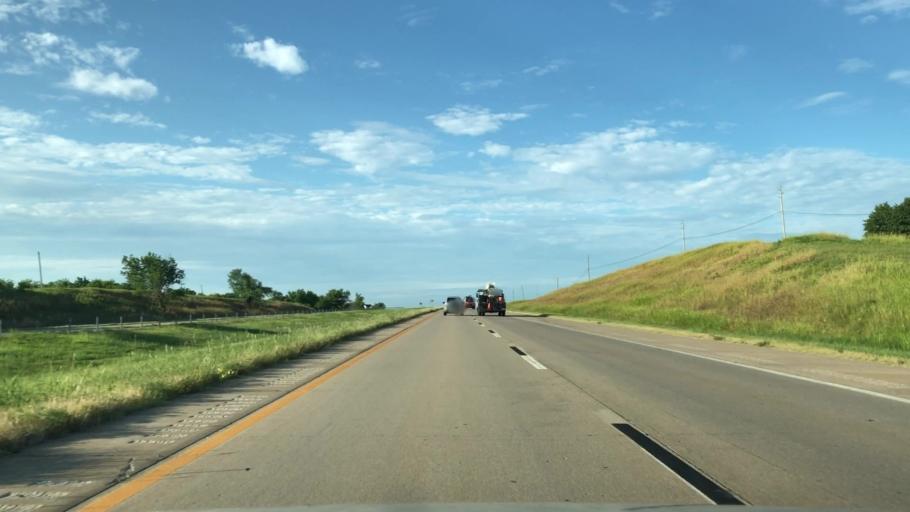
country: US
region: Oklahoma
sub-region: Osage County
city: Skiatook
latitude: 36.4847
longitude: -95.9207
